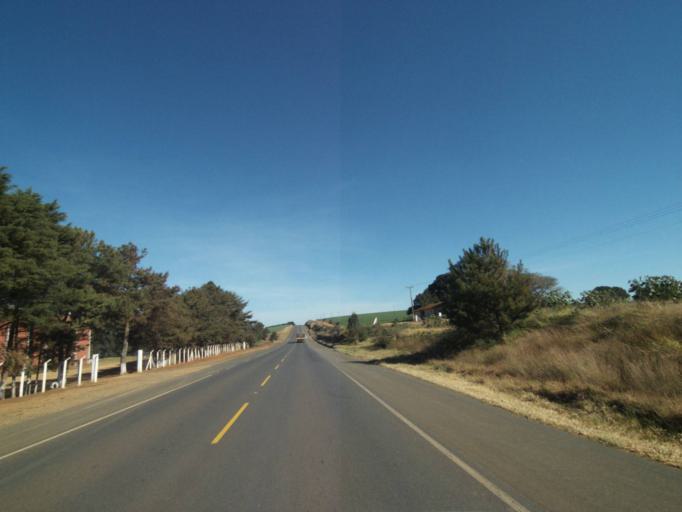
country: BR
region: Parana
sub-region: Tibagi
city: Tibagi
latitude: -24.3584
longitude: -50.3187
